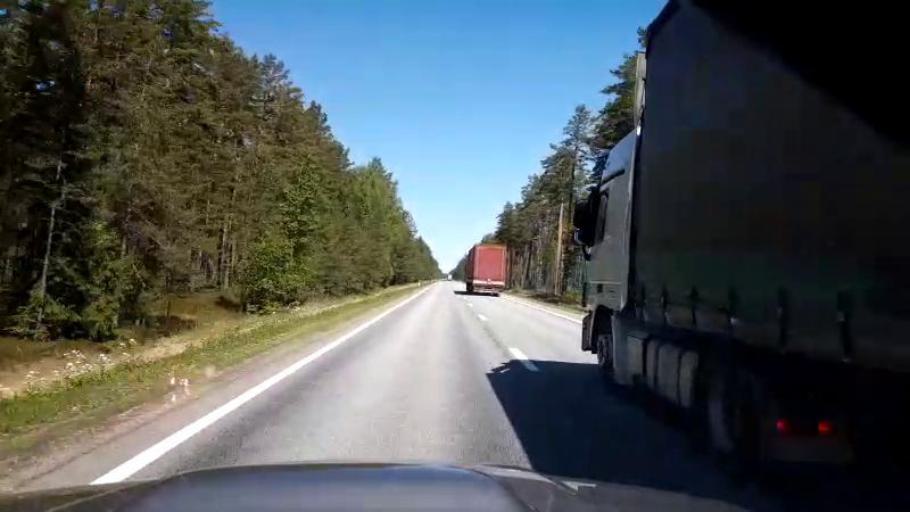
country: LV
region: Salacgrivas
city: Salacgriva
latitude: 57.5451
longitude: 24.4323
